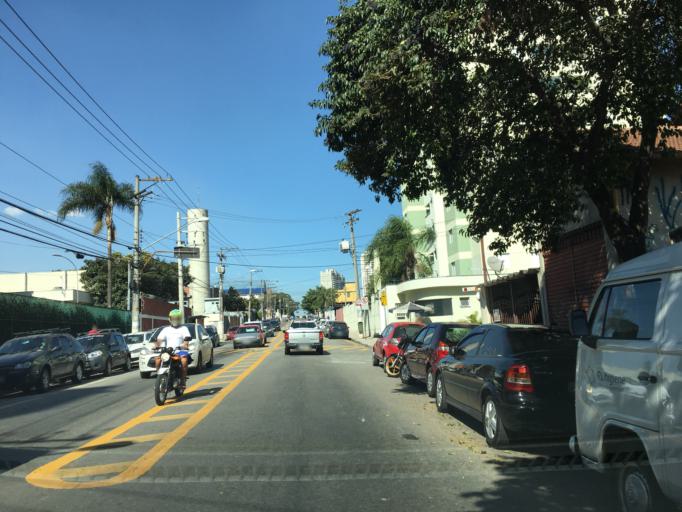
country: BR
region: Sao Paulo
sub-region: Osasco
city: Osasco
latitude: -23.5704
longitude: -46.7449
